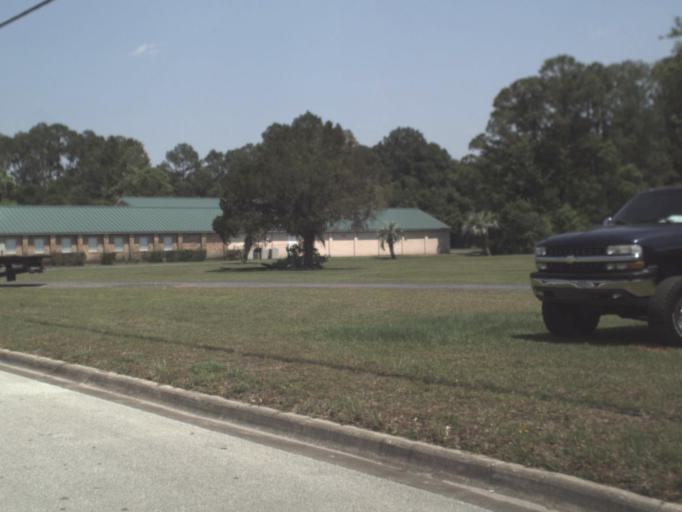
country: US
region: Florida
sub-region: Clay County
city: Bellair-Meadowbrook Terrace
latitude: 30.2880
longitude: -81.7973
